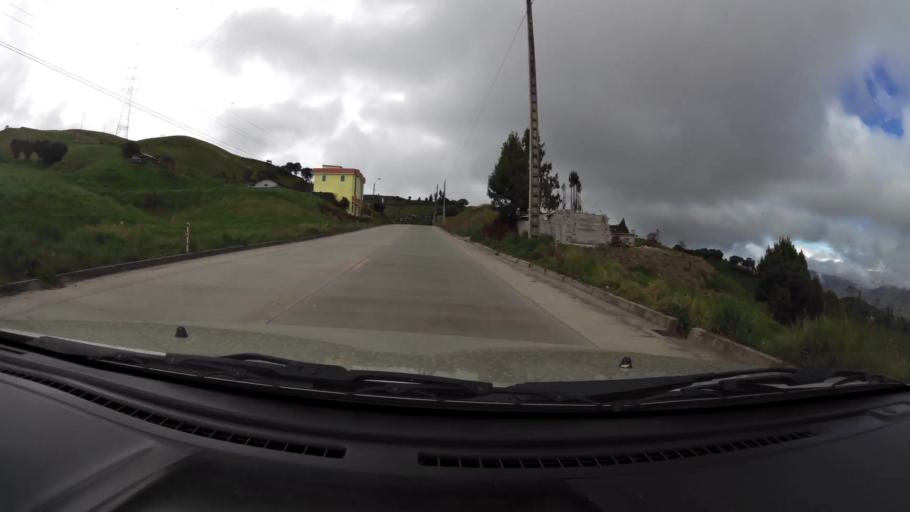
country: EC
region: Canar
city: Canar
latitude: -2.6212
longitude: -78.9166
